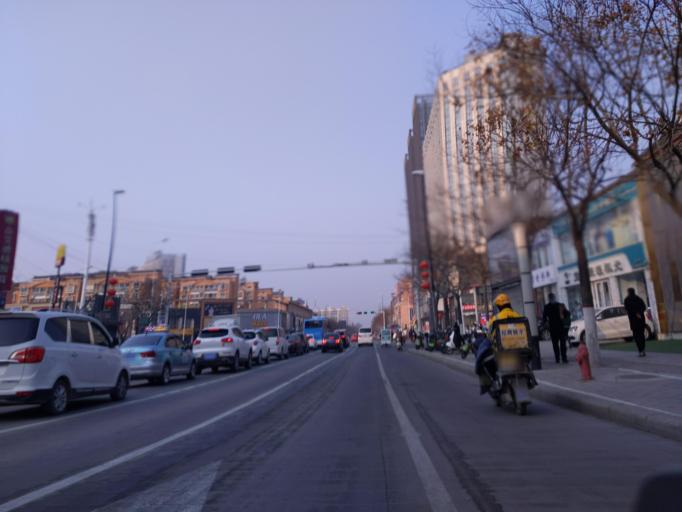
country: CN
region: Henan Sheng
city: Zhongyuanlu
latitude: 35.7696
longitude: 115.0586
